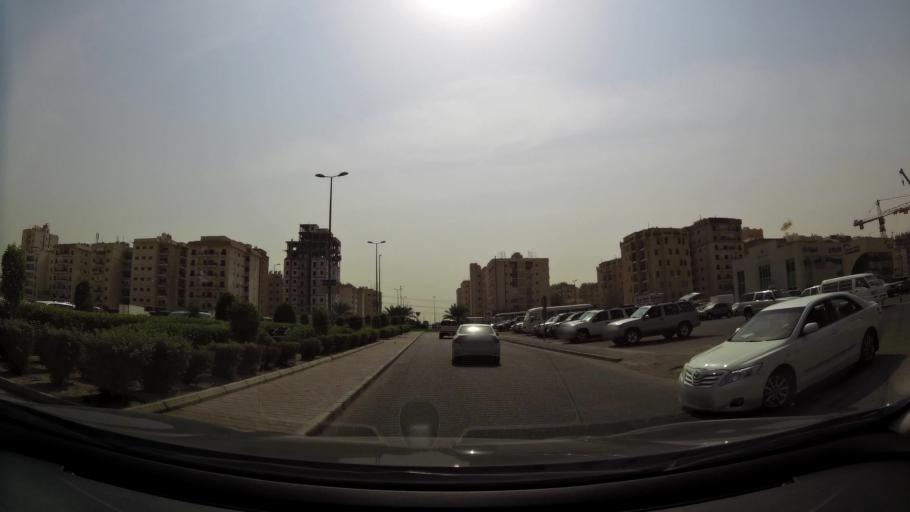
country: KW
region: Al Asimah
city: Ar Rabiyah
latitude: 29.3040
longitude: 47.9149
